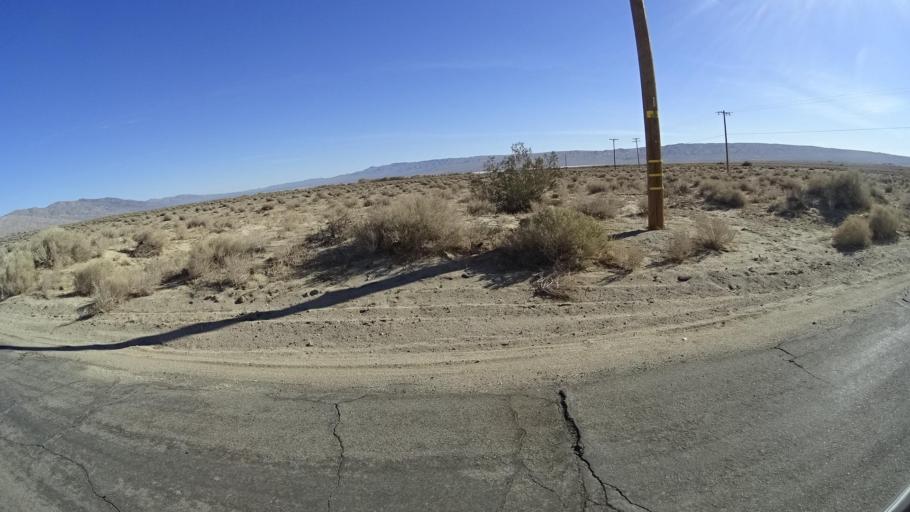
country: US
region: California
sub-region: Kern County
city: California City
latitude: 35.3094
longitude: -117.9504
